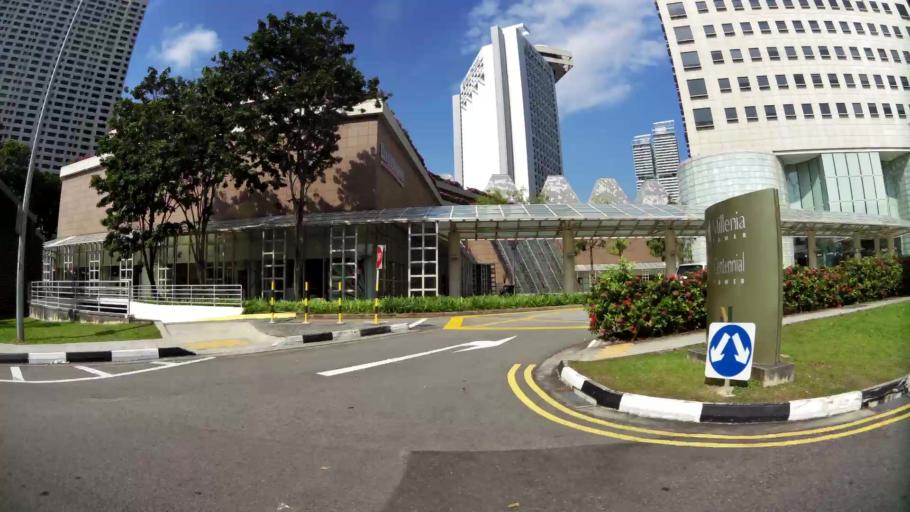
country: SG
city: Singapore
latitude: 1.2923
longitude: 103.8608
